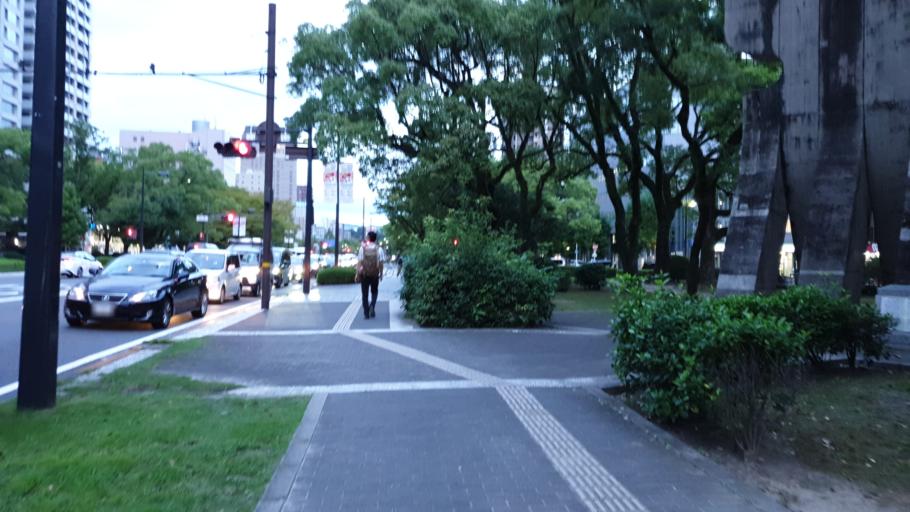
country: JP
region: Hiroshima
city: Hiroshima-shi
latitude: 34.3890
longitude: 132.4583
